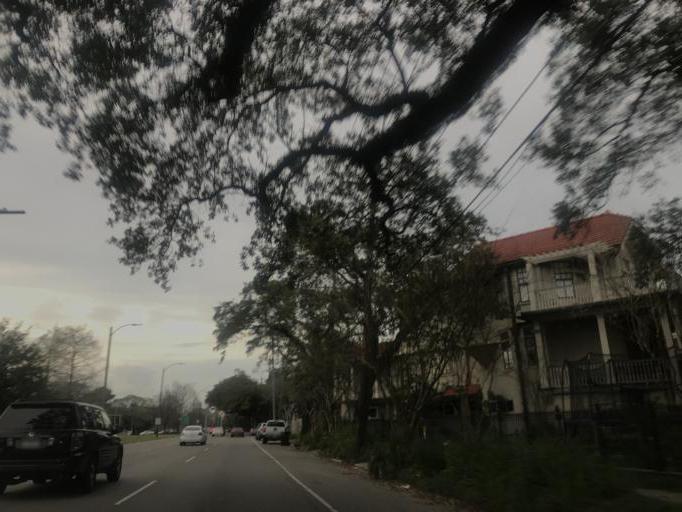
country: US
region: Louisiana
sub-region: Orleans Parish
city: New Orleans
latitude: 29.9496
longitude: -90.1151
